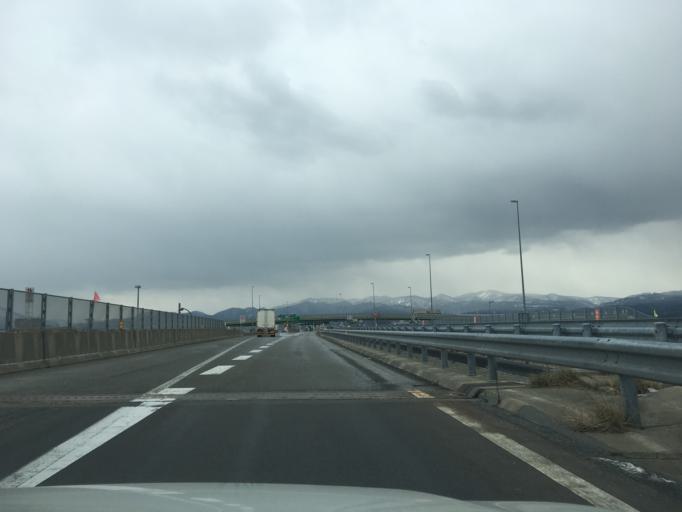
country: JP
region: Aomori
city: Aomori Shi
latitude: 40.7968
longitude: 140.7390
